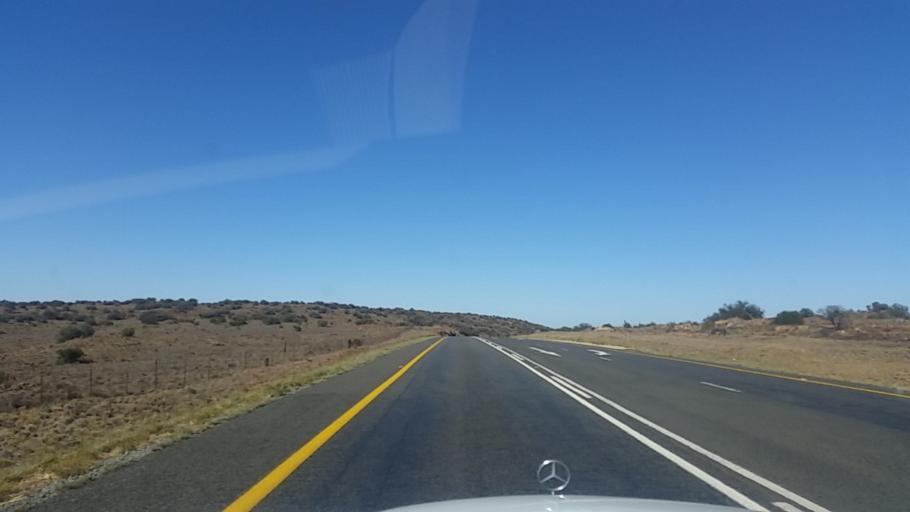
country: ZA
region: Eastern Cape
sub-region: Cacadu District Municipality
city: Graaff-Reinet
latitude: -32.0540
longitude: 24.6137
